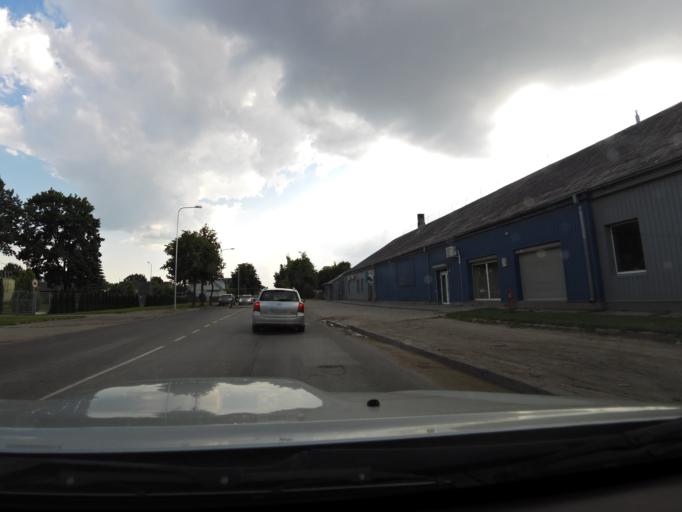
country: LT
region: Siauliu apskritis
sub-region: Siauliai
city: Siauliai
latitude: 55.9509
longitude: 23.3138
